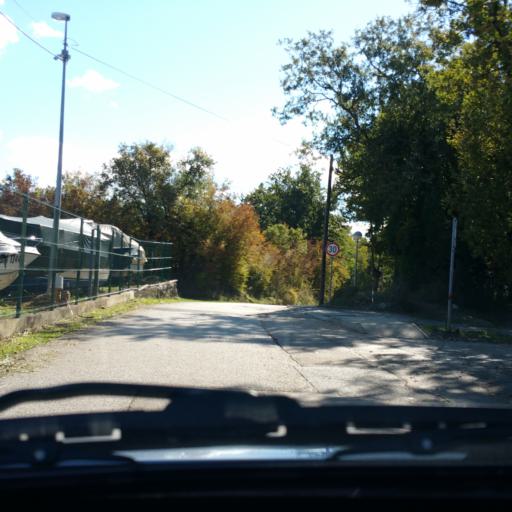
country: HR
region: Primorsko-Goranska
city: Njivice
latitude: 45.1714
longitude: 14.5486
